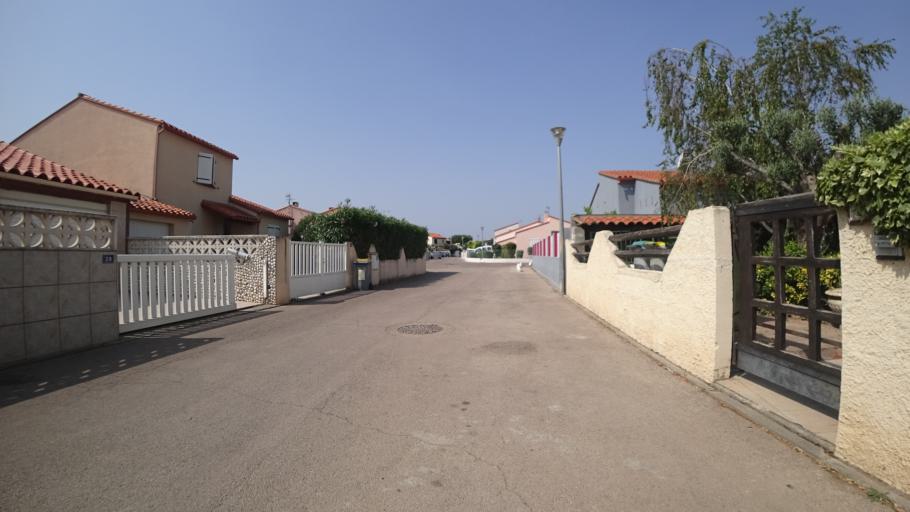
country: FR
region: Languedoc-Roussillon
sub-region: Departement des Pyrenees-Orientales
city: Saint-Laurent-de-la-Salanque
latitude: 42.7712
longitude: 3.0078
